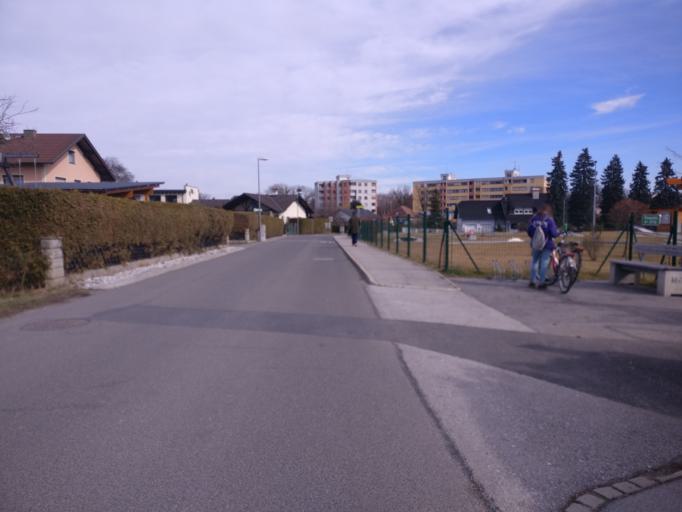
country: AT
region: Styria
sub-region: Politischer Bezirk Graz-Umgebung
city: Feldkirchen bei Graz
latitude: 47.0139
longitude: 15.4469
